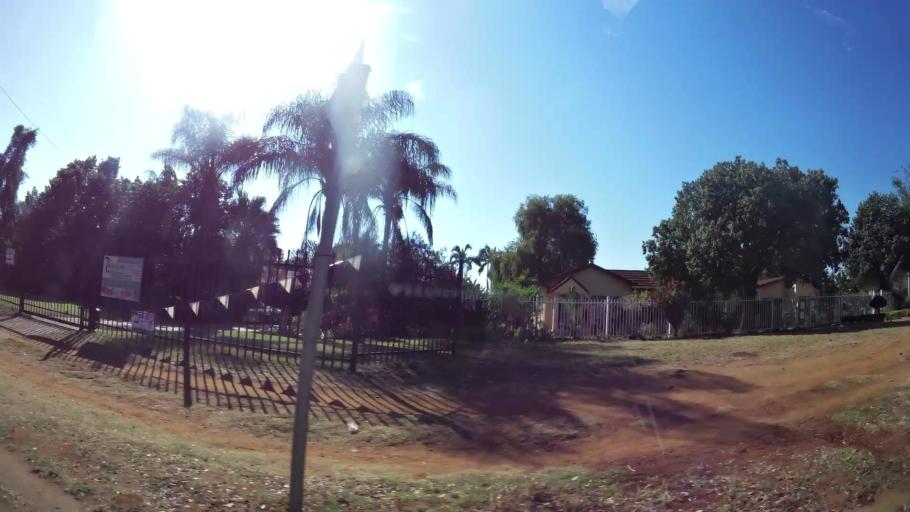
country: ZA
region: Gauteng
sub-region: City of Tshwane Metropolitan Municipality
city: Pretoria
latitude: -25.6762
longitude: 28.2156
